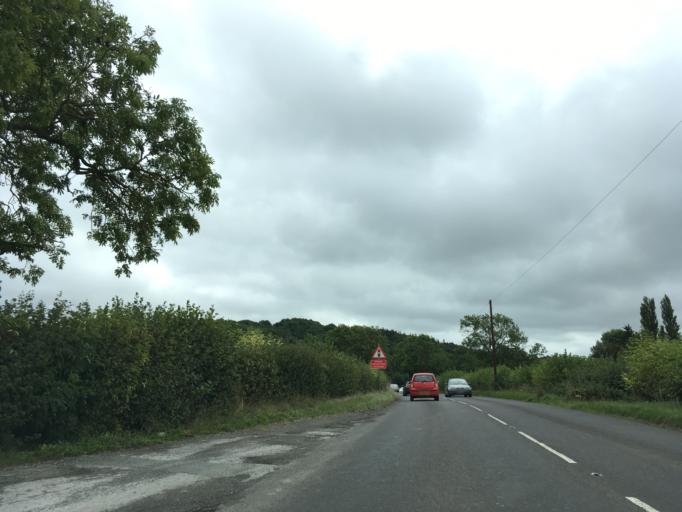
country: GB
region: England
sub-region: Bath and North East Somerset
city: Saltford
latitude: 51.3759
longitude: -2.4795
